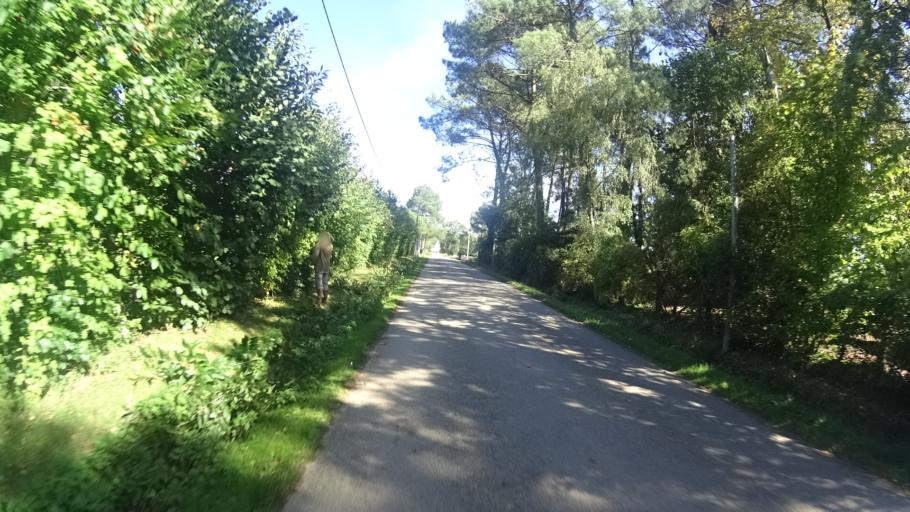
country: FR
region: Brittany
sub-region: Departement du Morbihan
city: Saint-Vincent-sur-Oust
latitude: 47.7339
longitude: -2.1598
